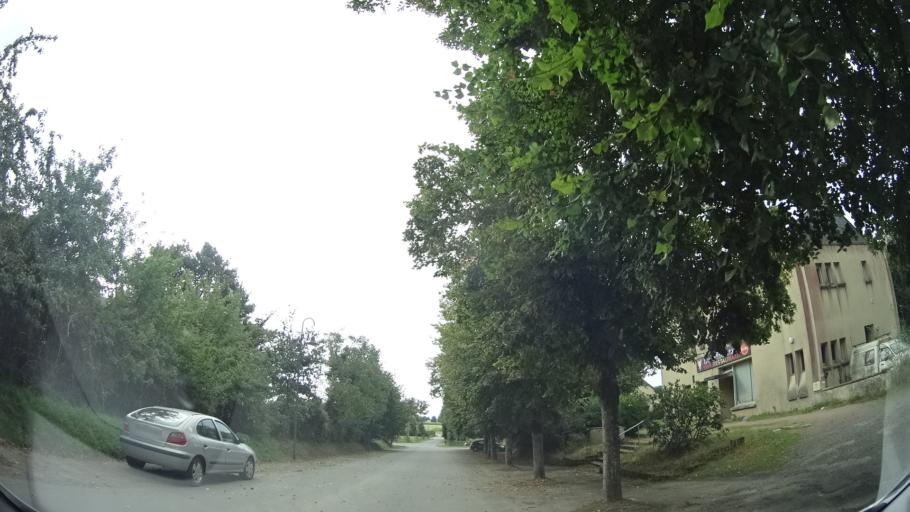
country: FR
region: Brittany
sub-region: Departement d'Ille-et-Vilaine
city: Tinteniac
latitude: 48.2848
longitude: -1.8888
